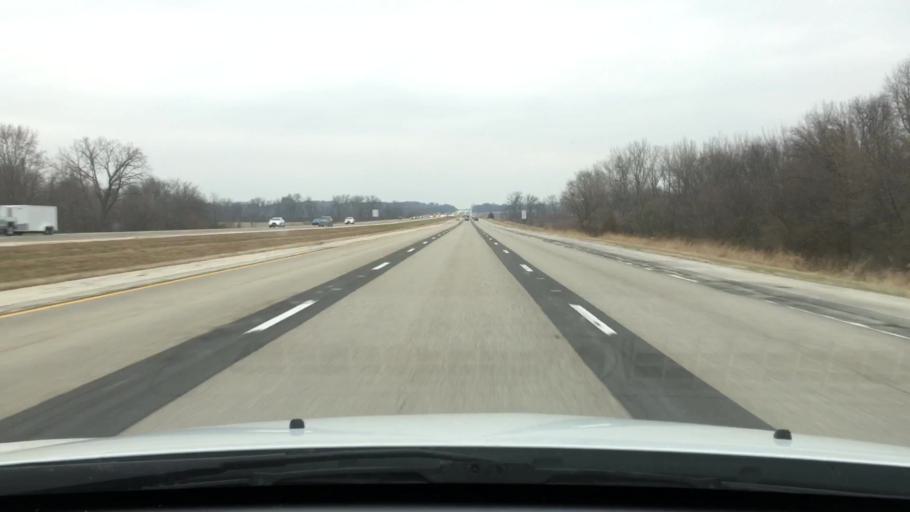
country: US
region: Illinois
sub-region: Logan County
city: Lincoln
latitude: 40.1202
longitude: -89.4165
